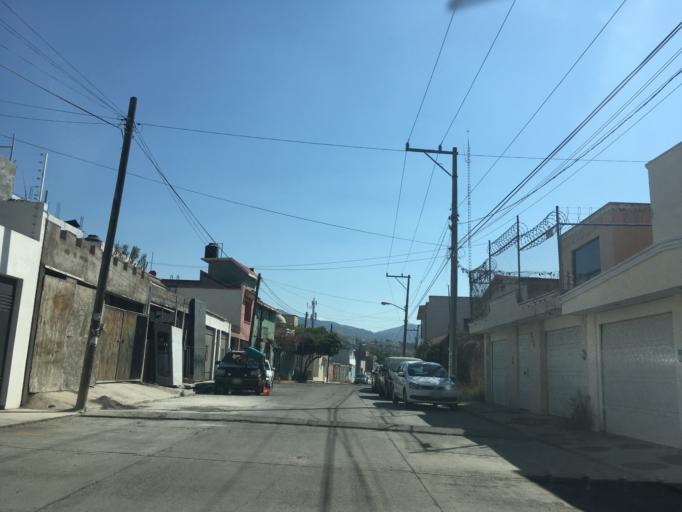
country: MX
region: Michoacan
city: Morelia
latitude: 19.6751
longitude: -101.2093
